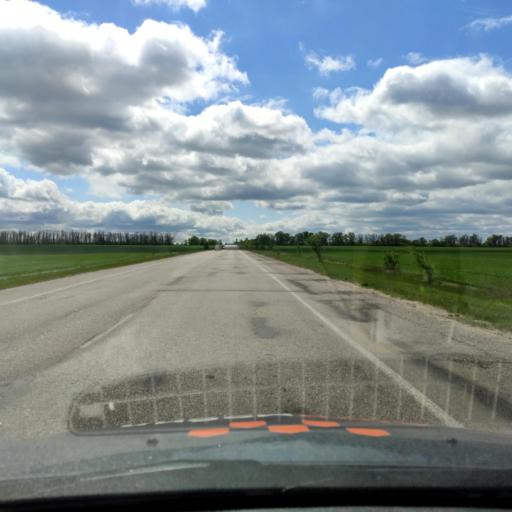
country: RU
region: Voronezj
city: Novaya Usman'
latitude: 51.5949
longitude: 39.3384
